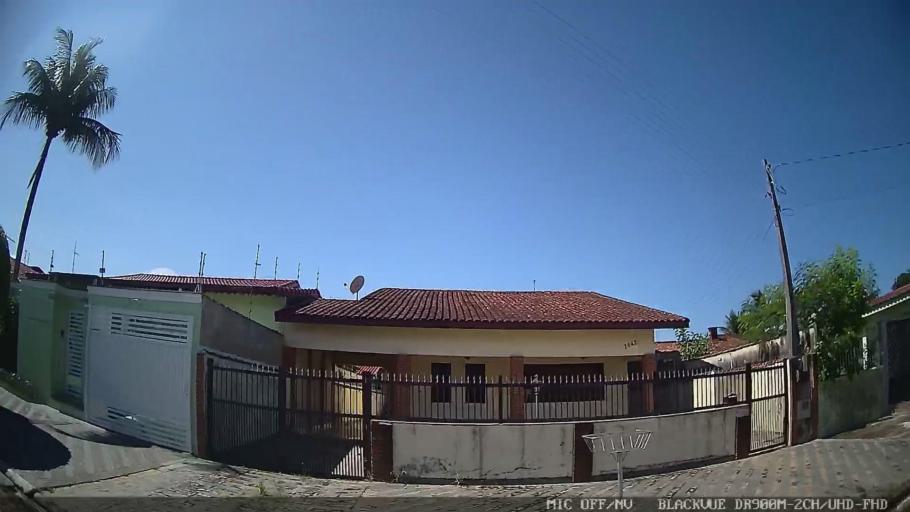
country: BR
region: Sao Paulo
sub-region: Peruibe
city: Peruibe
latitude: -24.3119
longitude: -46.9971
